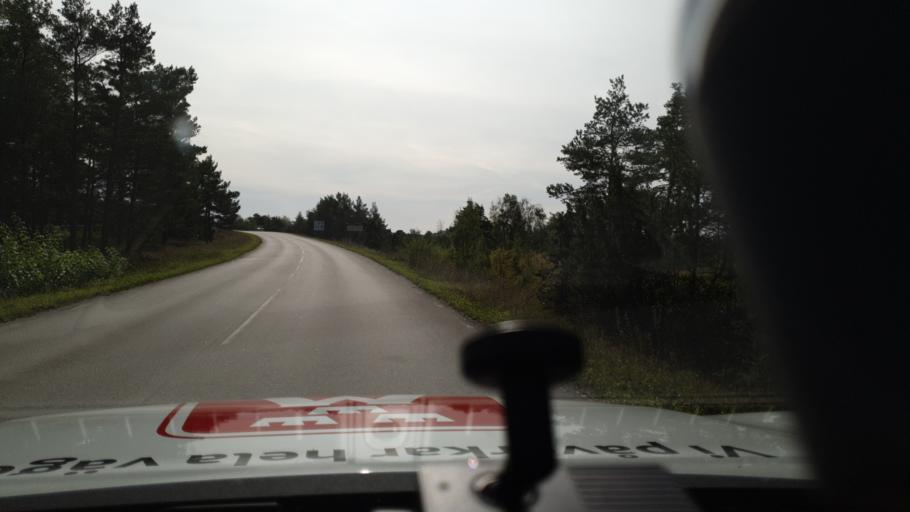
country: SE
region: Gotland
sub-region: Gotland
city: Slite
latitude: 57.8746
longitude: 19.0852
